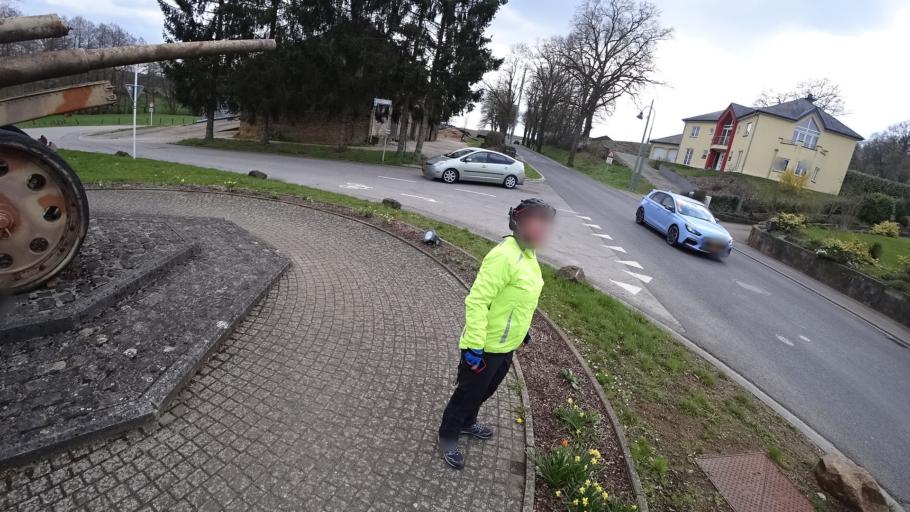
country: LU
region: Diekirch
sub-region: Canton de Redange
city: Useldange
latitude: 49.7637
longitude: 5.9756
